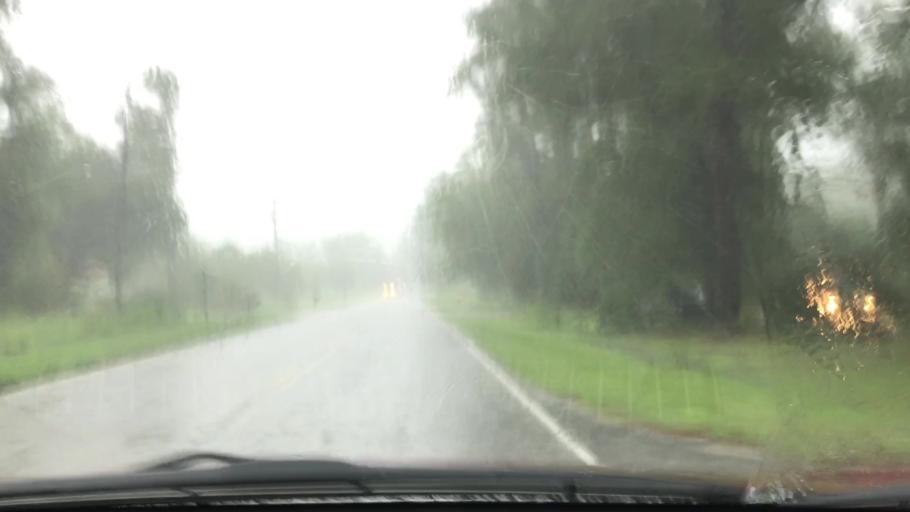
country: US
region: South Carolina
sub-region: Horry County
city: Red Hill
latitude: 33.8832
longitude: -78.9647
